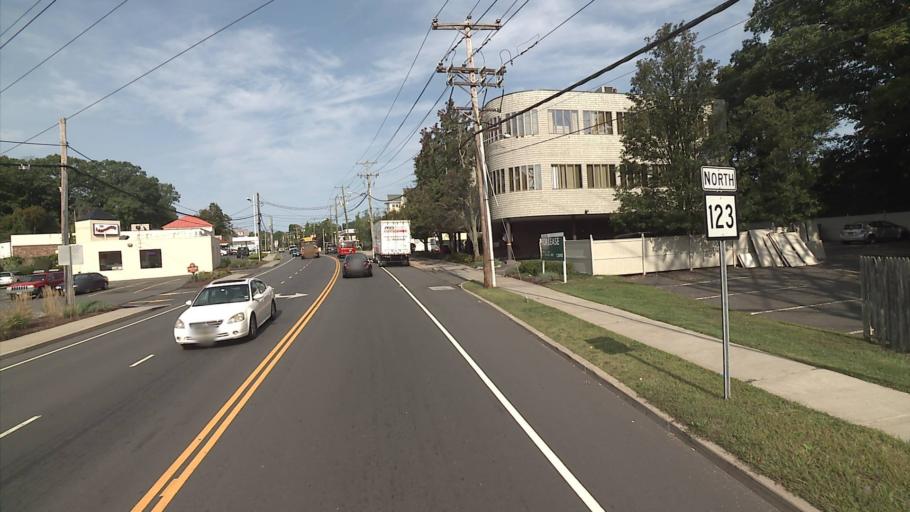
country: US
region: Connecticut
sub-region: Fairfield County
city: Norwalk
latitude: 41.1266
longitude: -73.4301
